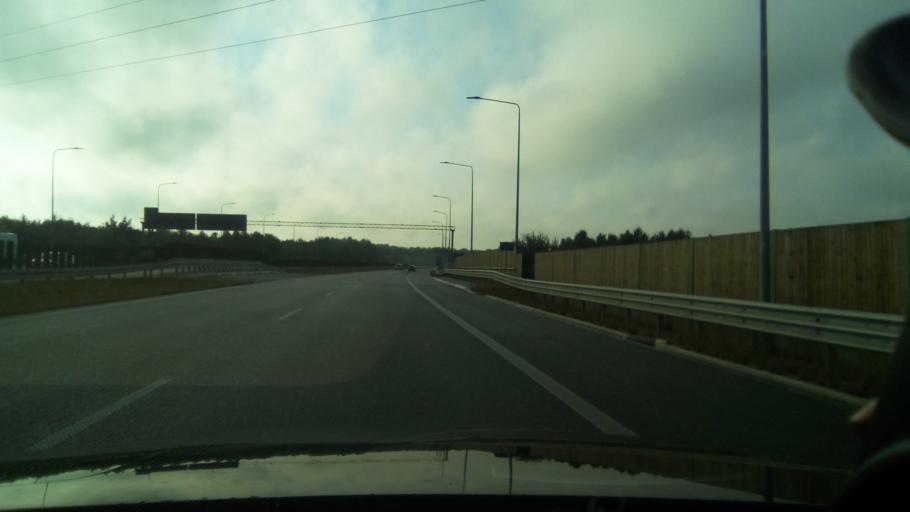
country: PL
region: Silesian Voivodeship
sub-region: Powiat czestochowski
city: Konopiska
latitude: 50.7420
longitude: 19.0493
